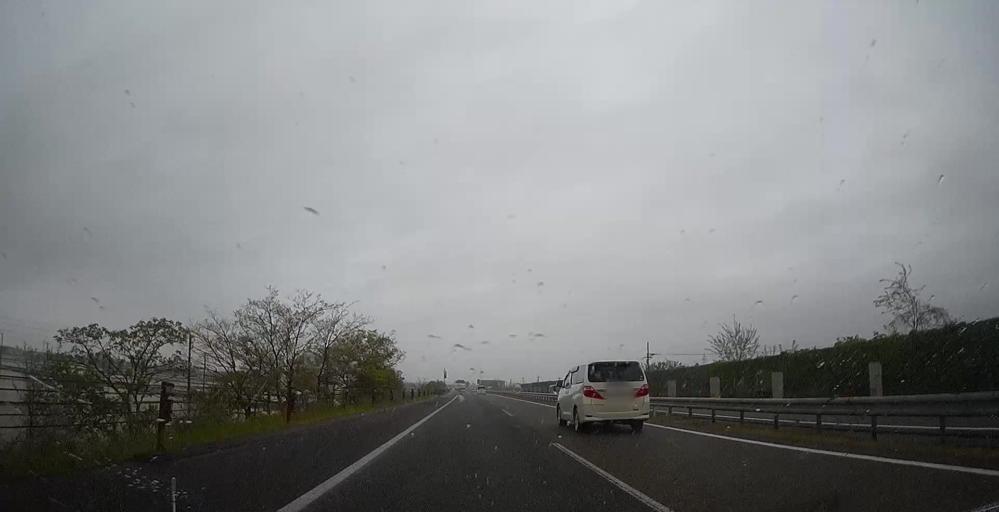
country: JP
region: Niigata
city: Sanjo
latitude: 37.6157
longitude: 138.9195
